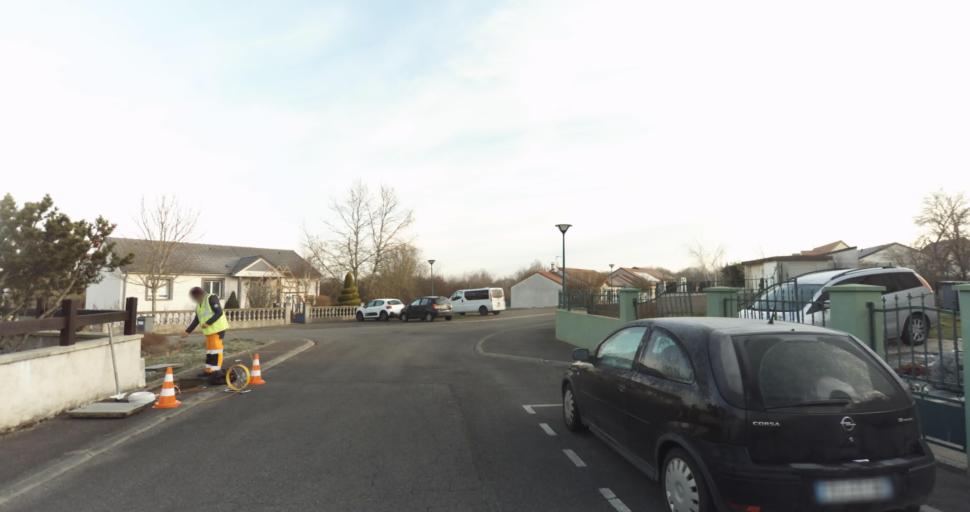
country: FR
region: Lorraine
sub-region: Departement de Meurthe-et-Moselle
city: Labry
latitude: 49.1670
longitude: 5.8869
